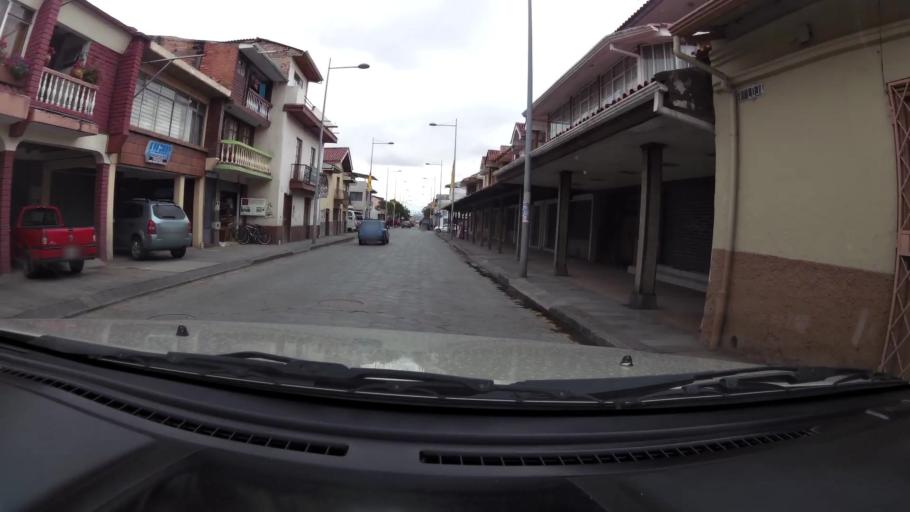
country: EC
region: Azuay
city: Cuenca
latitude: -2.9035
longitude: -79.0218
